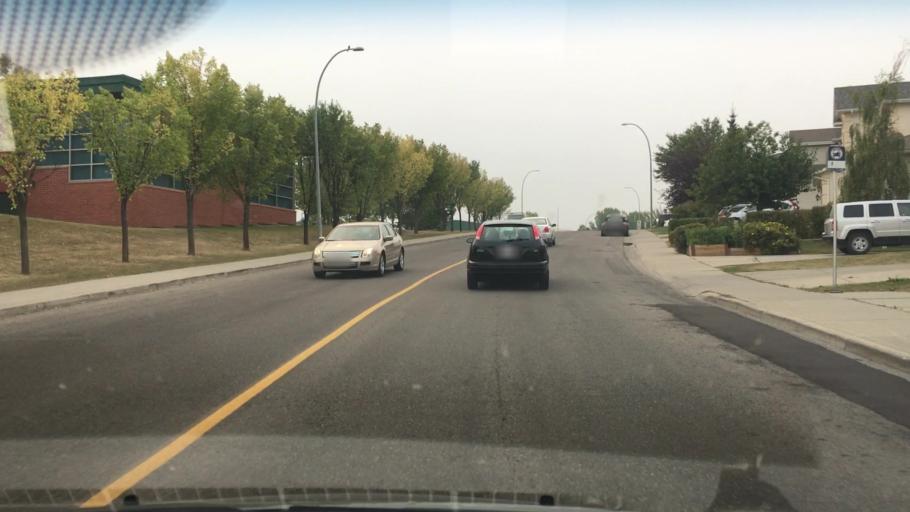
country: CA
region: Alberta
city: Calgary
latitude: 51.1509
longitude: -114.1162
